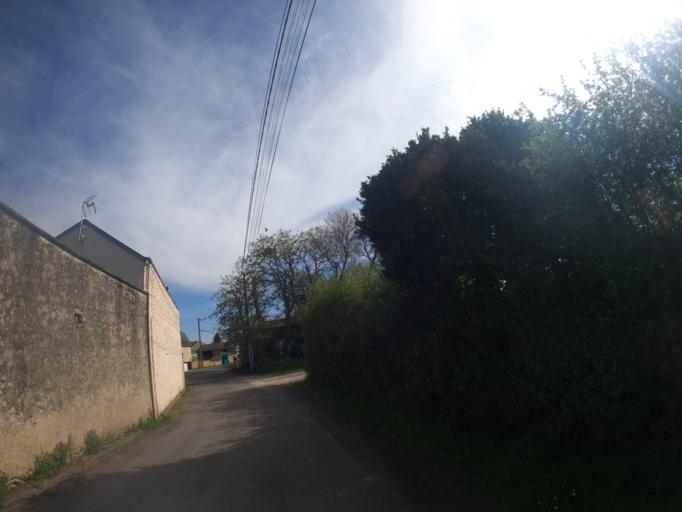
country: FR
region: Poitou-Charentes
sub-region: Departement des Deux-Sevres
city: Saint-Varent
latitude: 46.9264
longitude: -0.2221
